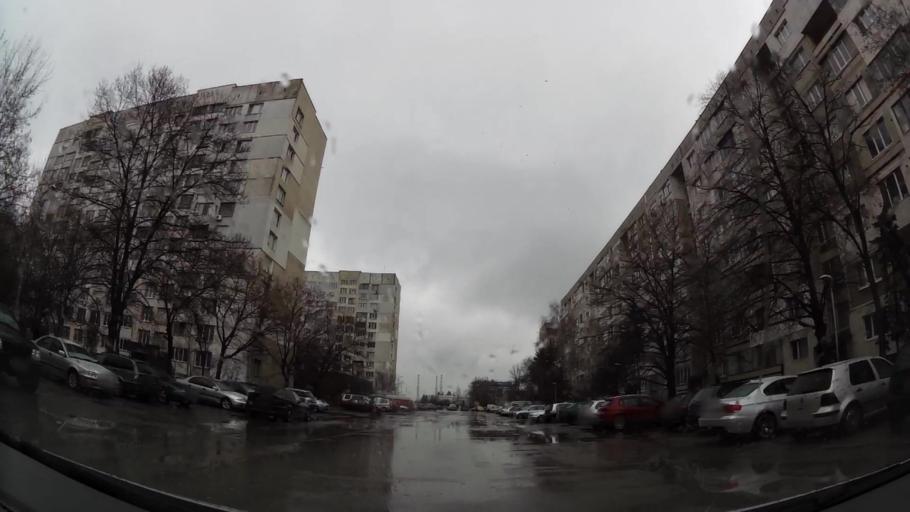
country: BG
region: Sofia-Capital
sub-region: Stolichna Obshtina
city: Sofia
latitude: 42.6603
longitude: 23.4002
